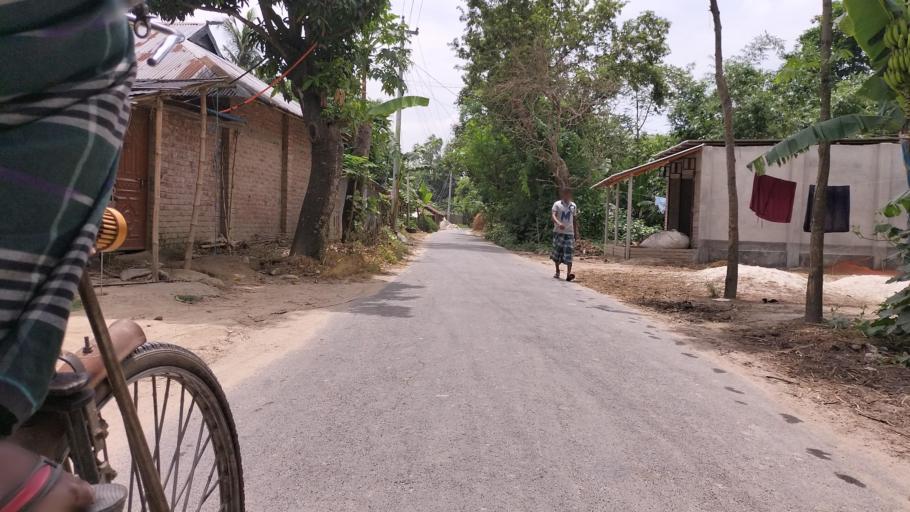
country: BD
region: Rajshahi
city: Rajshahi
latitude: 24.5152
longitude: 88.6286
